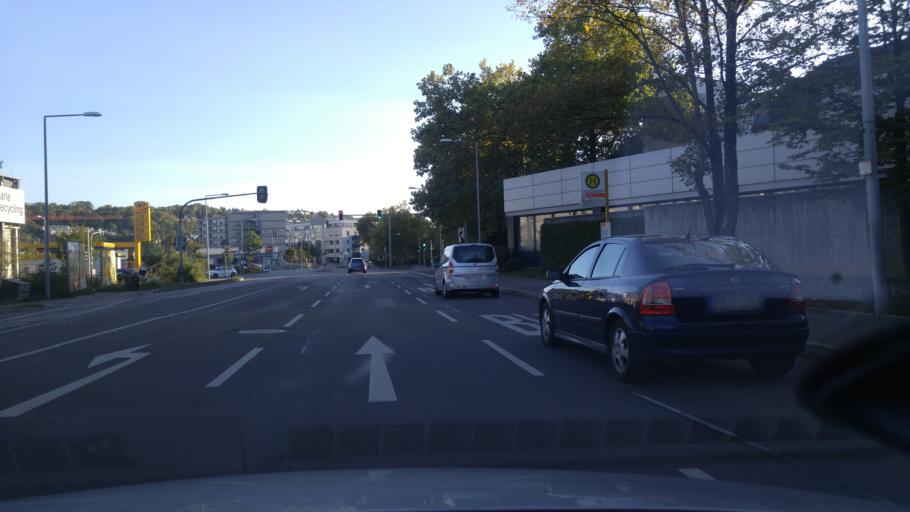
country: DE
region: Baden-Wuerttemberg
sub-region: Regierungsbezirk Stuttgart
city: Stuttgart Feuerbach
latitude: 48.8183
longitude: 9.1669
